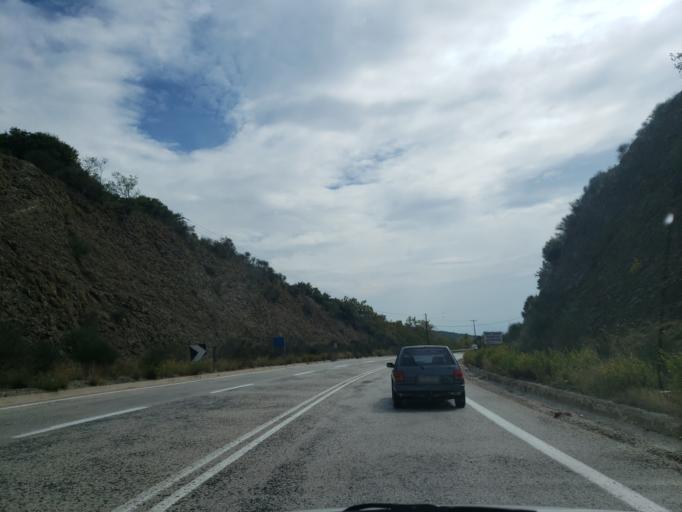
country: GR
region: Central Greece
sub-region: Nomos Fthiotidos
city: Stavros
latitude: 38.9876
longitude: 22.3771
